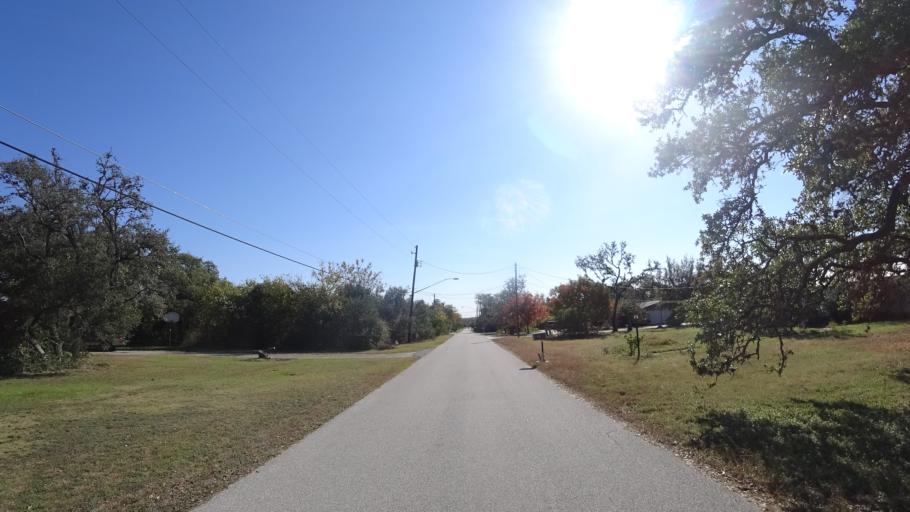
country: US
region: Texas
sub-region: Travis County
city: Barton Creek
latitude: 30.2294
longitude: -97.8576
